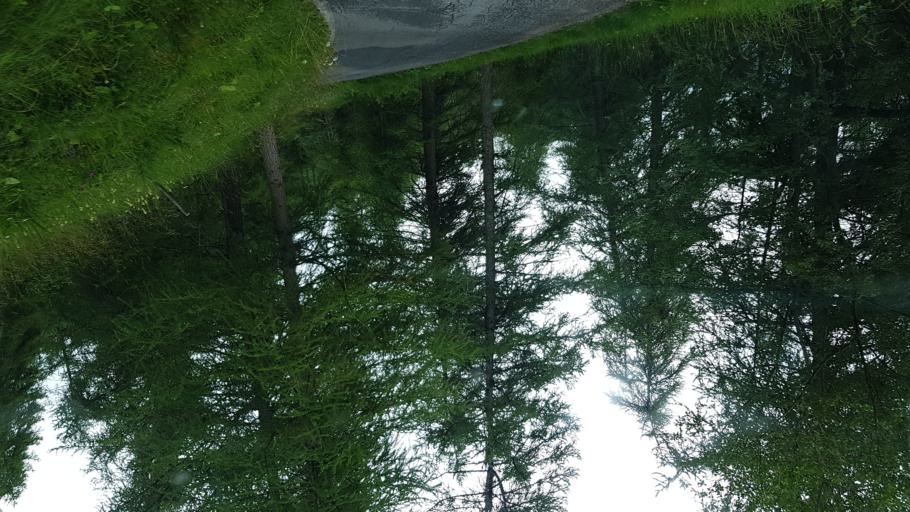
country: IT
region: Piedmont
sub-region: Provincia di Cuneo
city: Stroppo
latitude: 44.5167
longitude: 7.1068
